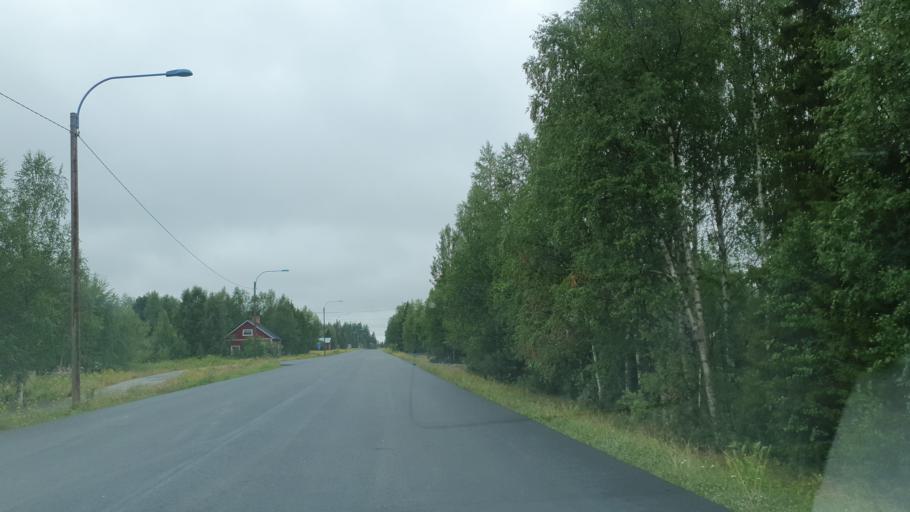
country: FI
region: Lapland
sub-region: Itae-Lappi
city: Pelkosenniemi
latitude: 67.1186
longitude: 27.4985
